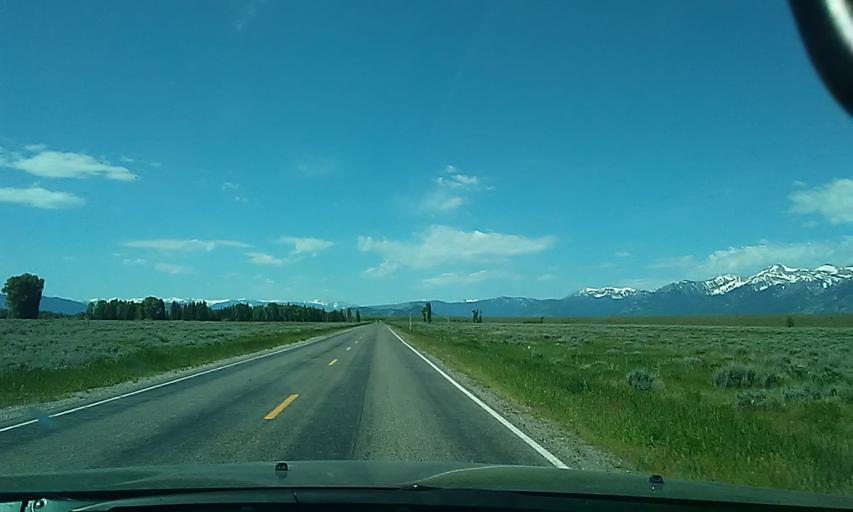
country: US
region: Wyoming
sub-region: Teton County
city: Jackson
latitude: 43.6125
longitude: -110.6816
